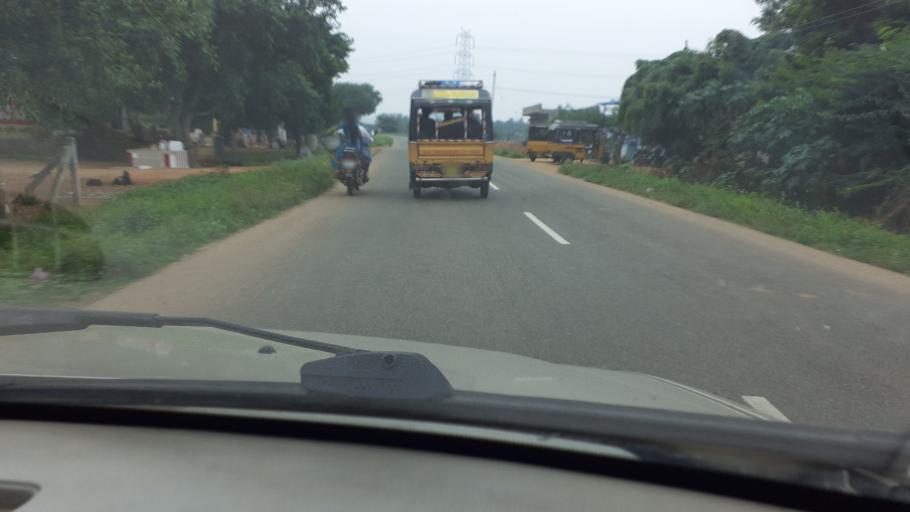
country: IN
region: Tamil Nadu
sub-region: Tirunelveli Kattabo
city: Nanguneri
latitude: 8.4899
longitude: 77.6462
